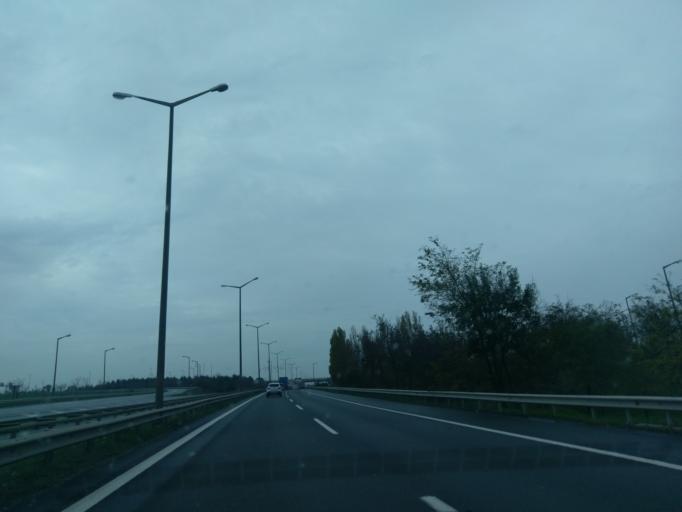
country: TR
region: Istanbul
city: Silivri
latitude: 41.1094
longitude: 28.2684
